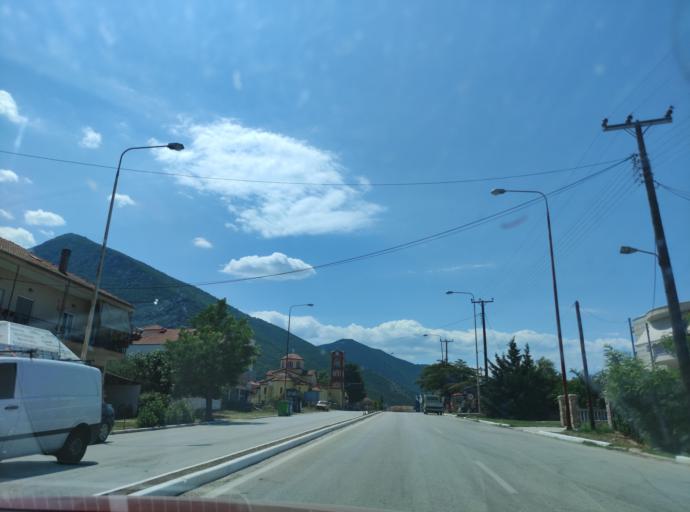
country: GR
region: East Macedonia and Thrace
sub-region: Nomos Kavalas
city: Nikisiani
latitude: 40.9711
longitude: 24.1493
